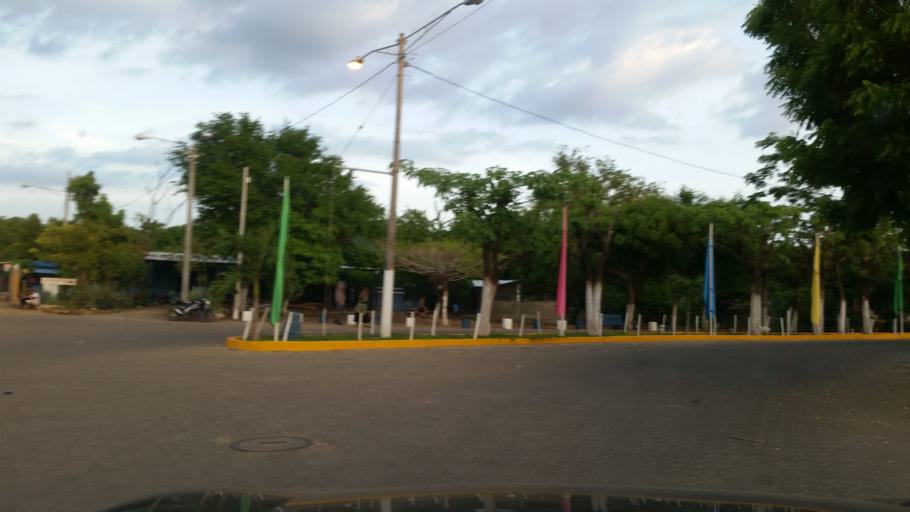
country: NI
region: Managua
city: Masachapa
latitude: 11.7757
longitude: -86.5050
